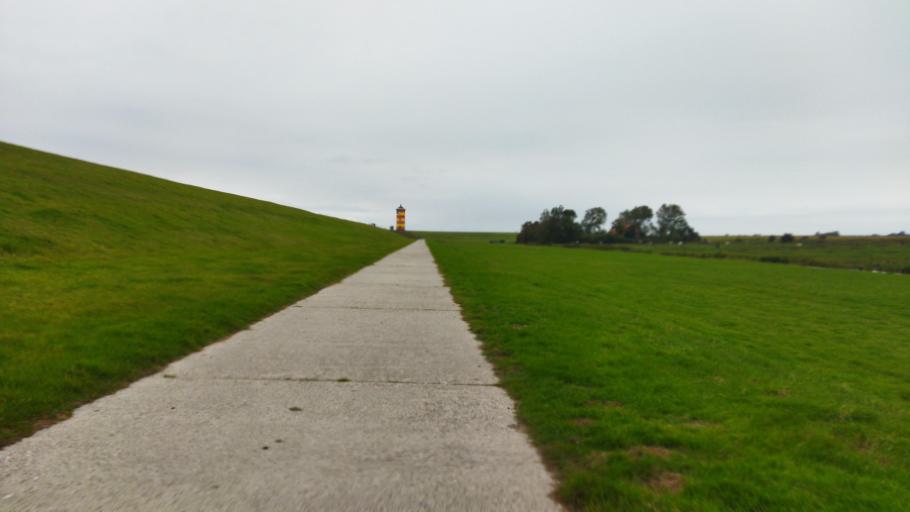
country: DE
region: Lower Saxony
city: Wirdum
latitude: 53.4950
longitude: 7.0436
